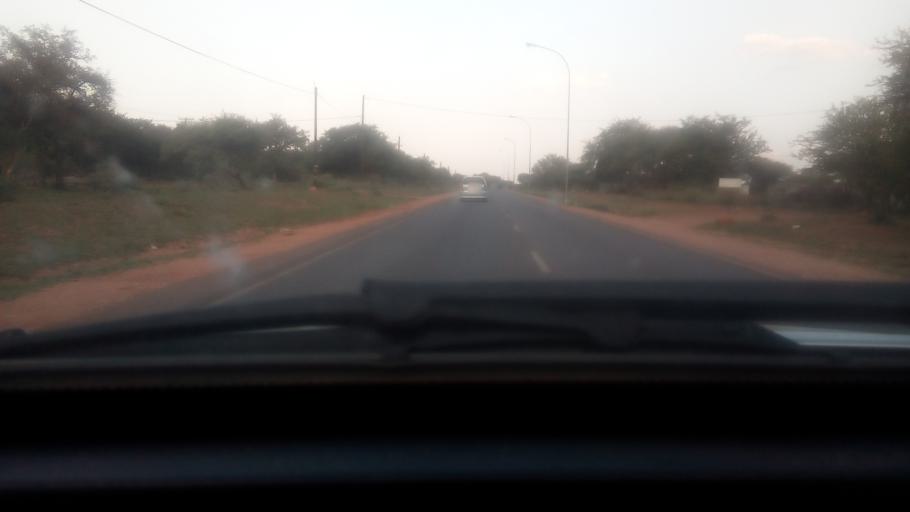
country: BW
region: Kgatleng
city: Bokaa
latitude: -24.4348
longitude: 26.0399
